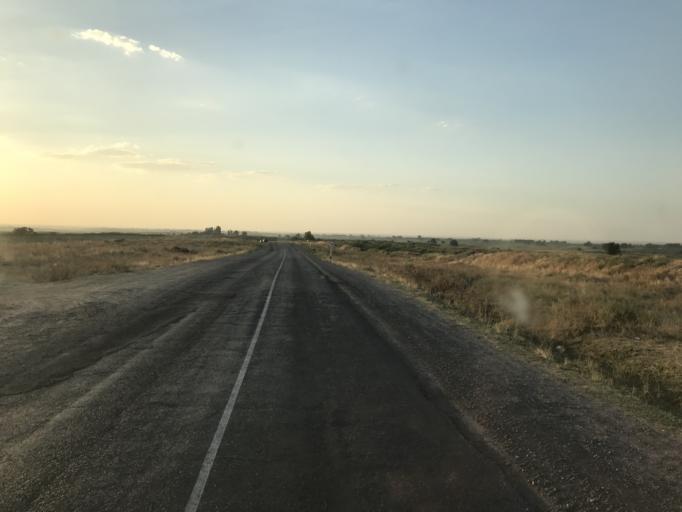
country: UZ
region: Toshkent
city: Yangiyul
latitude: 41.3398
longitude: 68.8788
